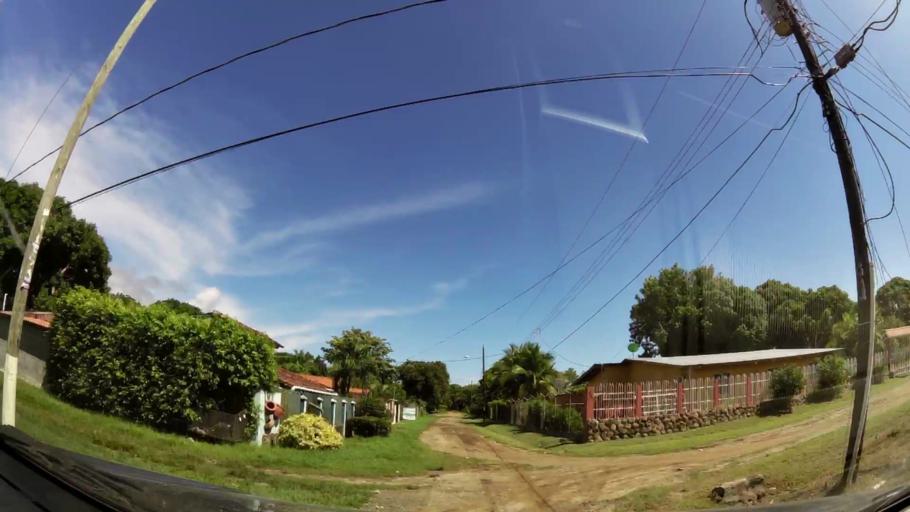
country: PA
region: Panama
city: Nueva Gorgona
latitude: 8.5590
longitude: -79.8731
